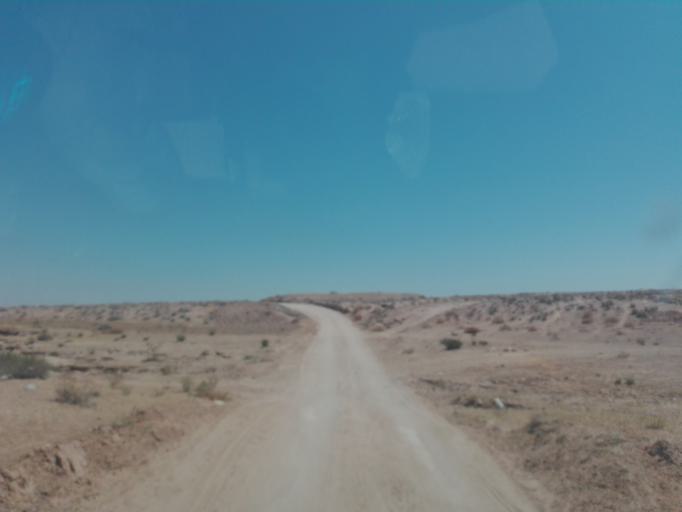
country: TN
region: Safaqis
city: Skhira
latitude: 34.3773
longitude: 9.9108
